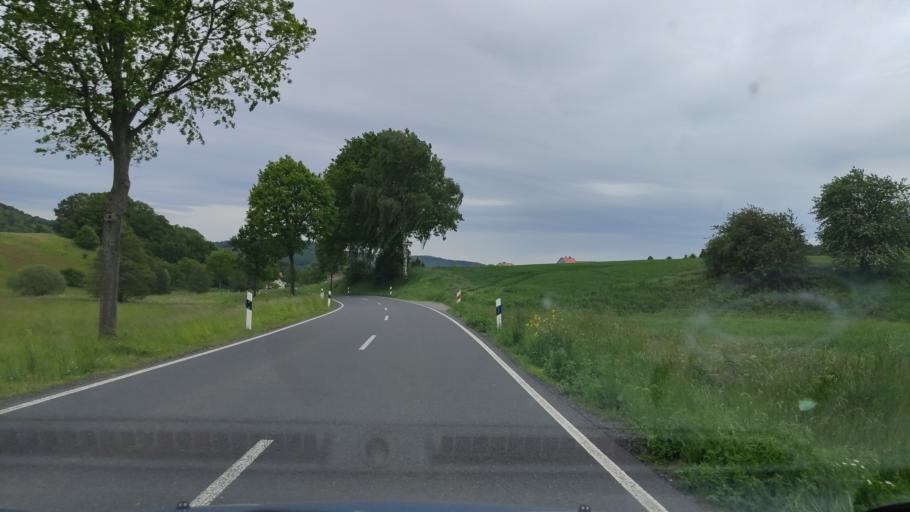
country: DE
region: Lower Saxony
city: Hardegsen
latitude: 51.6939
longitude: 9.7961
